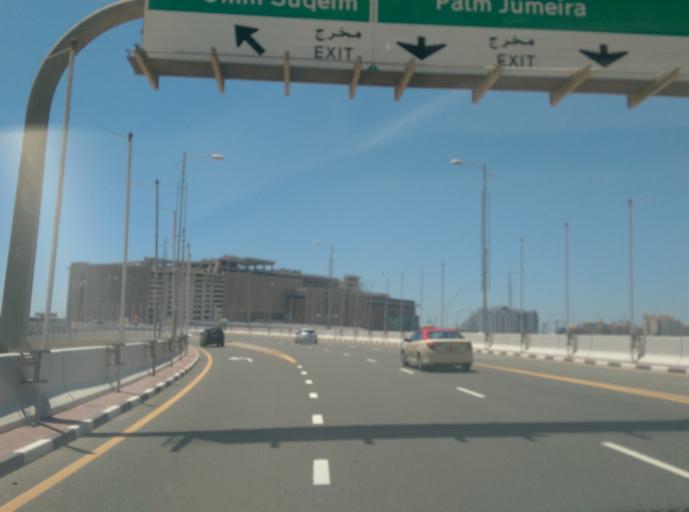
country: AE
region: Dubai
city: Dubai
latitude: 25.1008
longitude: 55.1603
